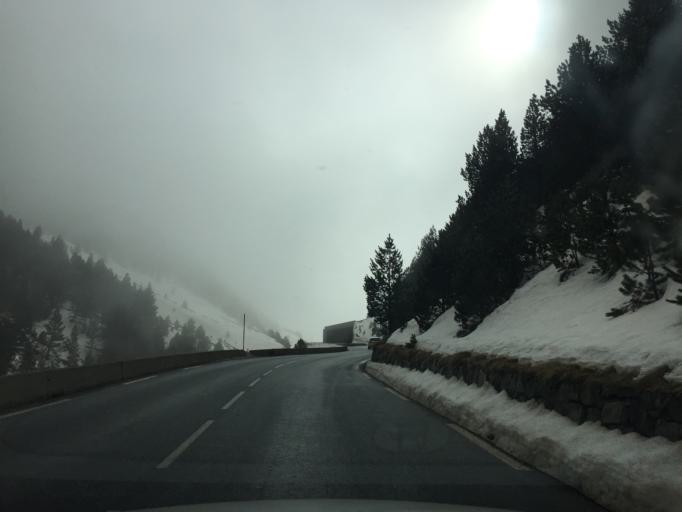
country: ES
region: Aragon
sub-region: Provincia de Huesca
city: Bielsa
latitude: 42.7639
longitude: 0.1973
